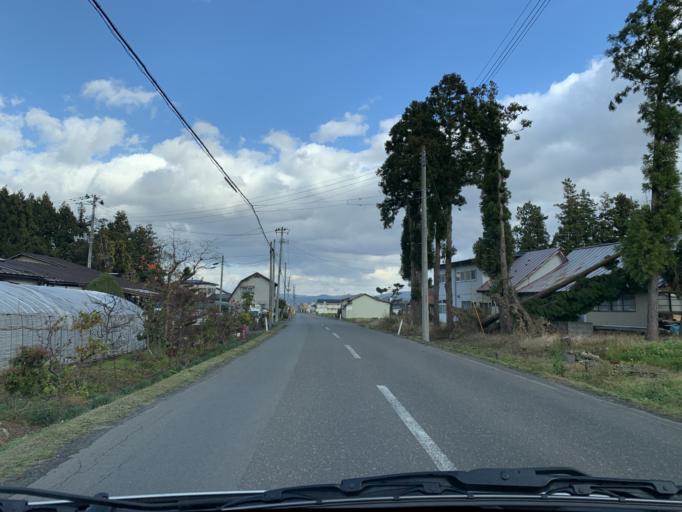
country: JP
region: Iwate
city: Mizusawa
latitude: 39.1329
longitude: 141.1118
